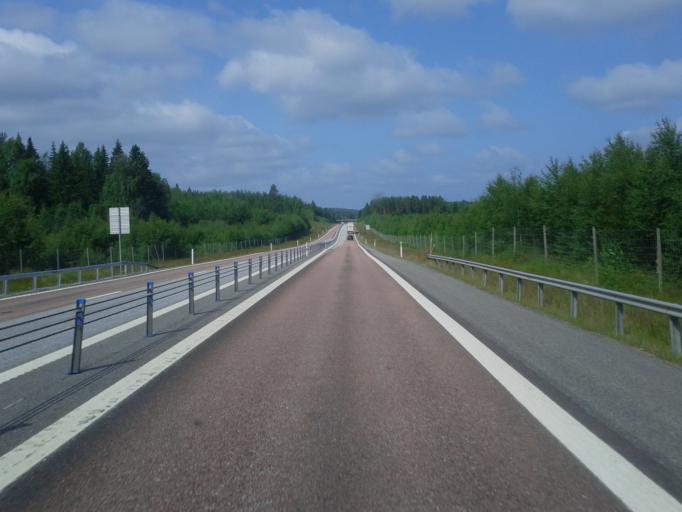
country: SE
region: Vaesterbotten
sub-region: Skelleftea Kommun
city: Soedra Bergsbyn
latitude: 64.6918
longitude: 21.0344
